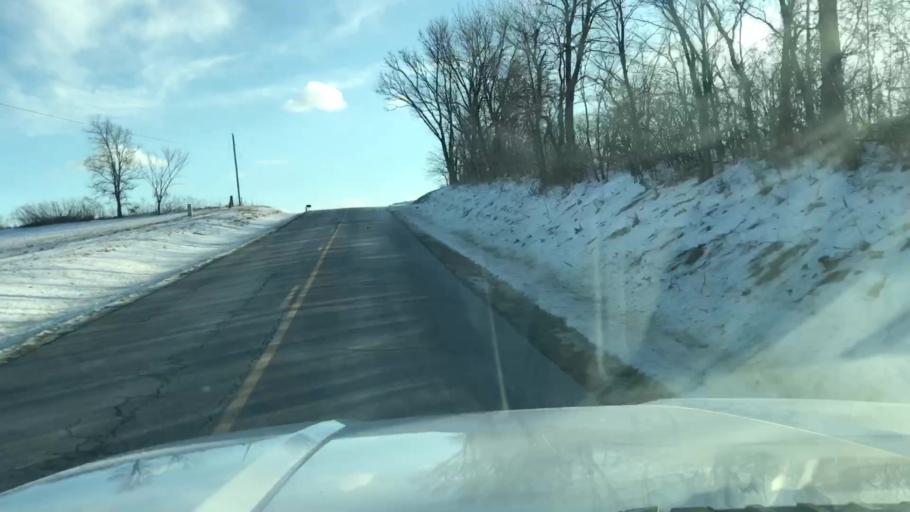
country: US
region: Missouri
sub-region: Holt County
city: Oregon
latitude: 40.0651
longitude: -94.9748
